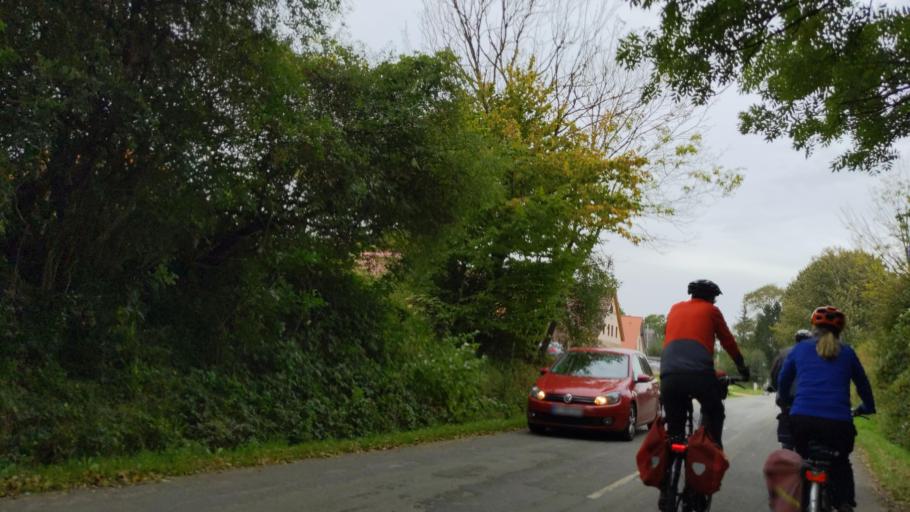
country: DE
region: Mecklenburg-Vorpommern
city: Schlagsdorf
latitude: 53.7578
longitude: 10.8277
